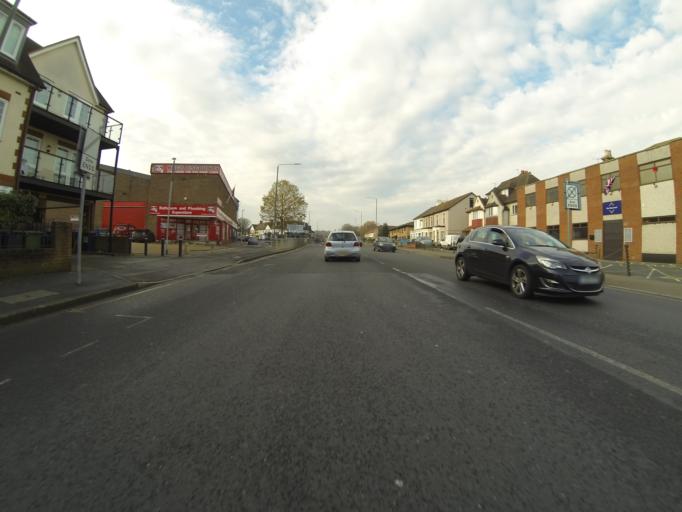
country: GB
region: England
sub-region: Greater London
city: Welling
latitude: 51.4642
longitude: 0.0965
